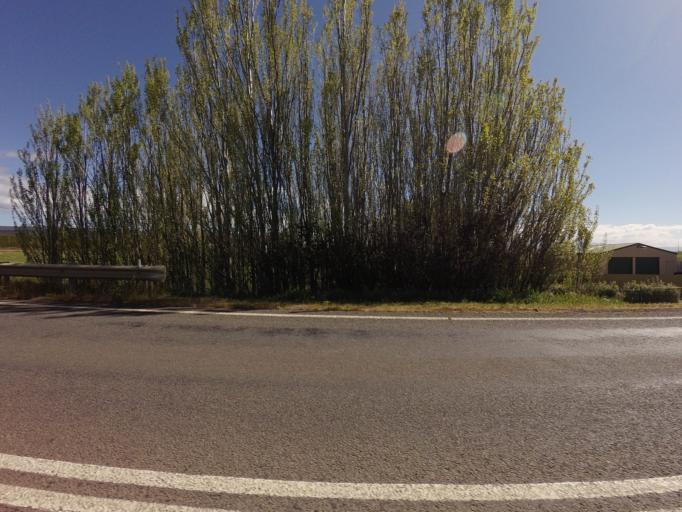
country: AU
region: Tasmania
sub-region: Derwent Valley
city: New Norfolk
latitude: -42.7078
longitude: 146.9451
